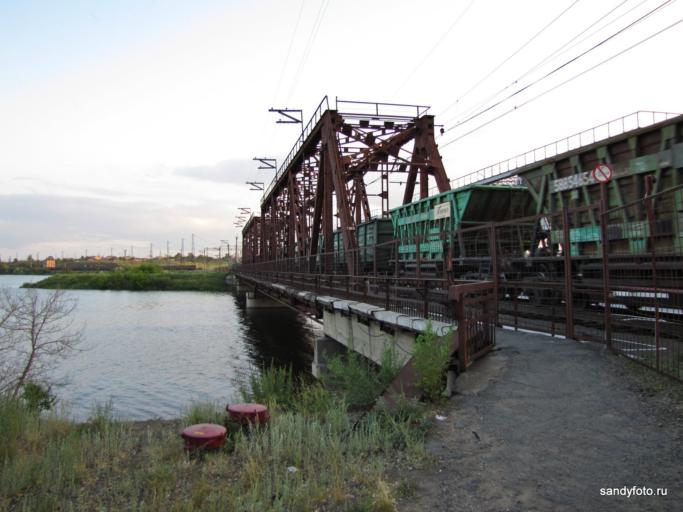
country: RU
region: Chelyabinsk
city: Troitsk
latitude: 54.0561
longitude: 61.6125
